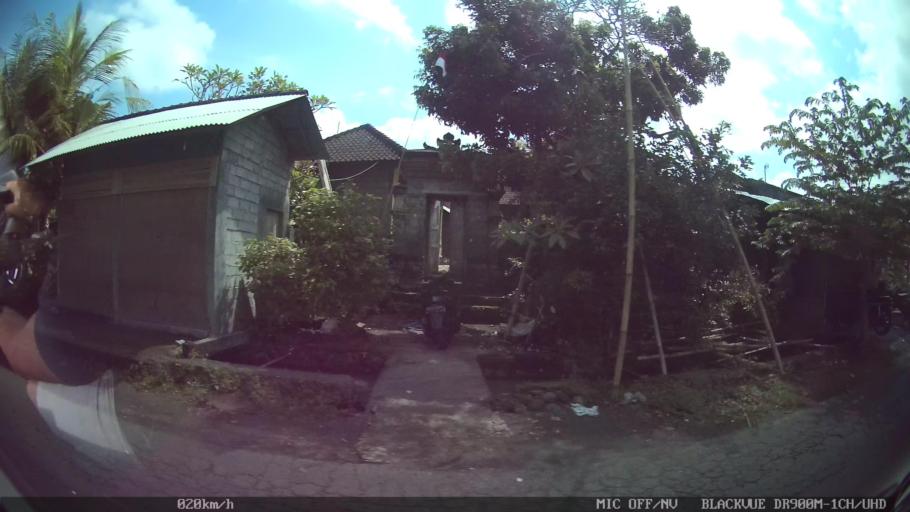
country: ID
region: Bali
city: Banjar Apuan Kaja
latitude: -8.5168
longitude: 115.3296
